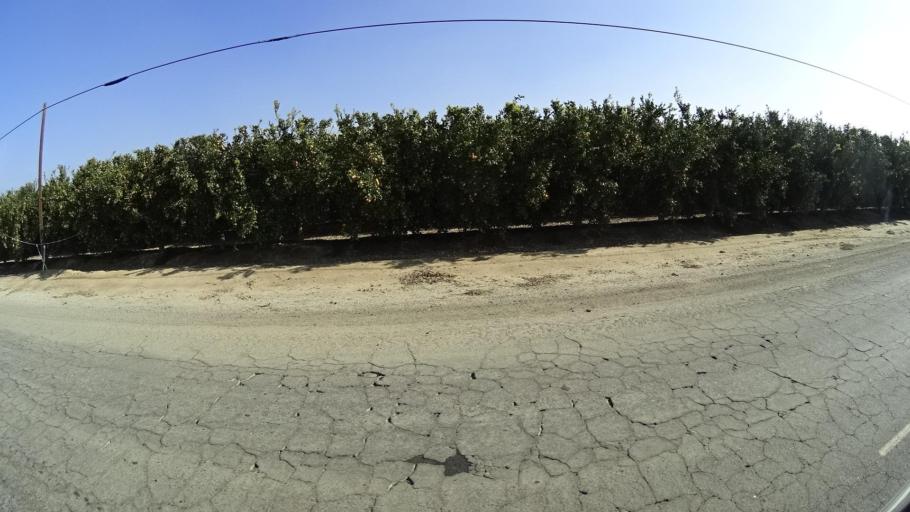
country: US
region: California
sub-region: Kern County
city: McFarland
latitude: 35.6620
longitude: -119.1339
